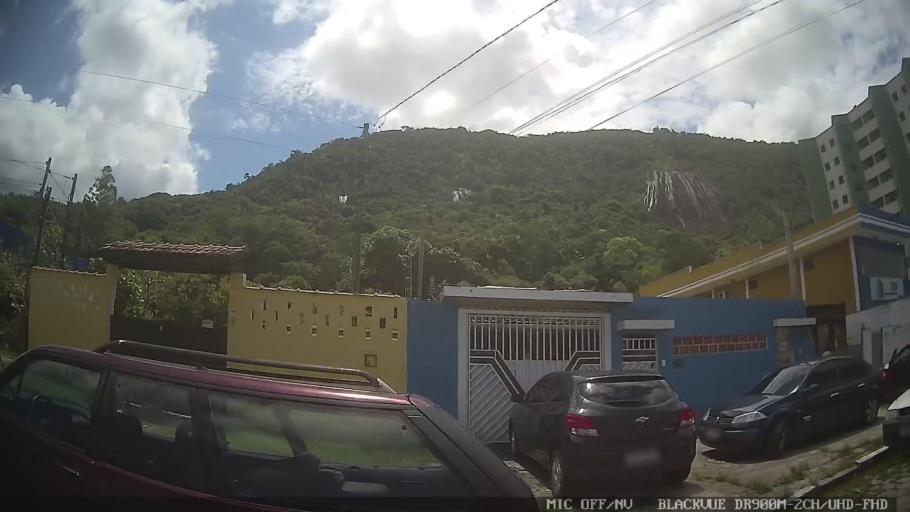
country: BR
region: Sao Paulo
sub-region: Caraguatatuba
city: Caraguatatuba
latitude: -23.6164
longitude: -45.4057
